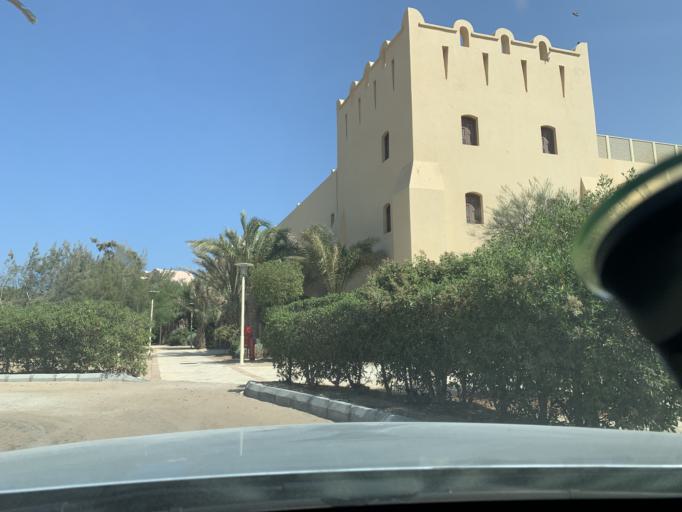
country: EG
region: Red Sea
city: El Gouna
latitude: 27.4012
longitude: 33.6725
